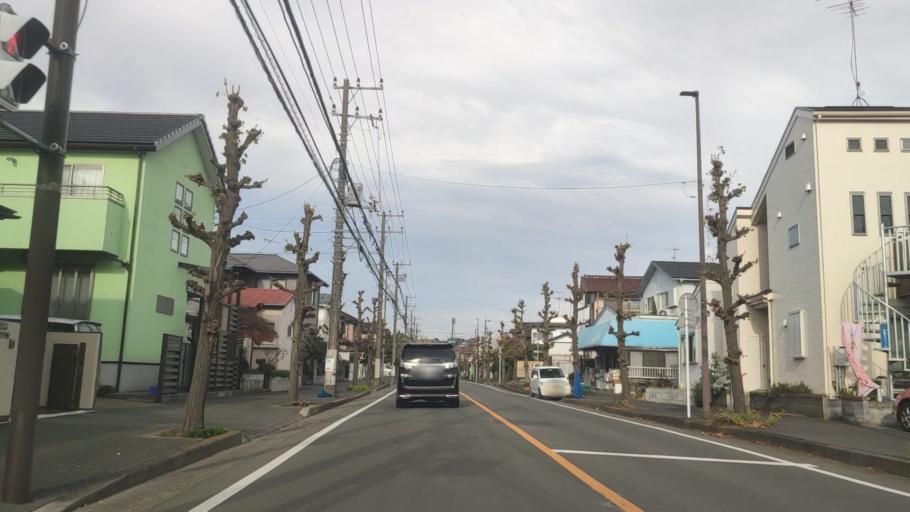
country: JP
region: Kanagawa
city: Atsugi
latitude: 35.4340
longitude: 139.4050
